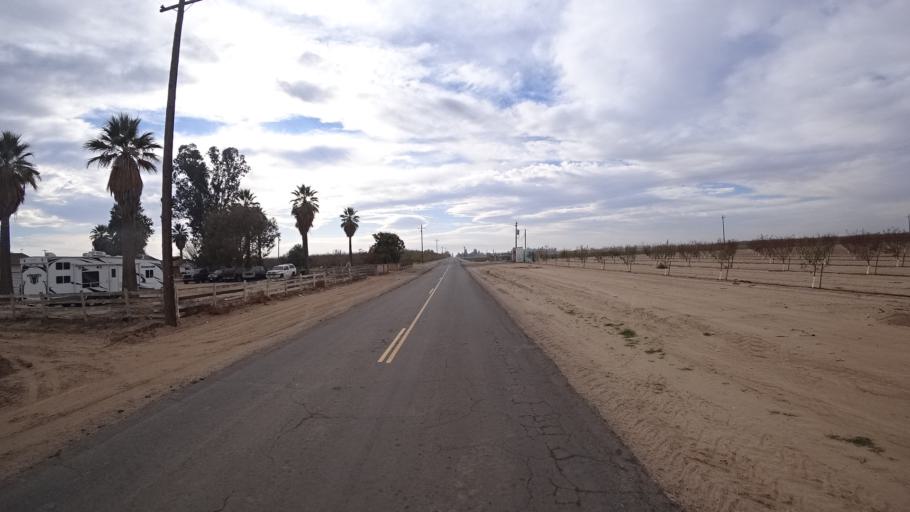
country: US
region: California
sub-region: Kern County
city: Rosedale
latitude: 35.4060
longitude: -119.1810
